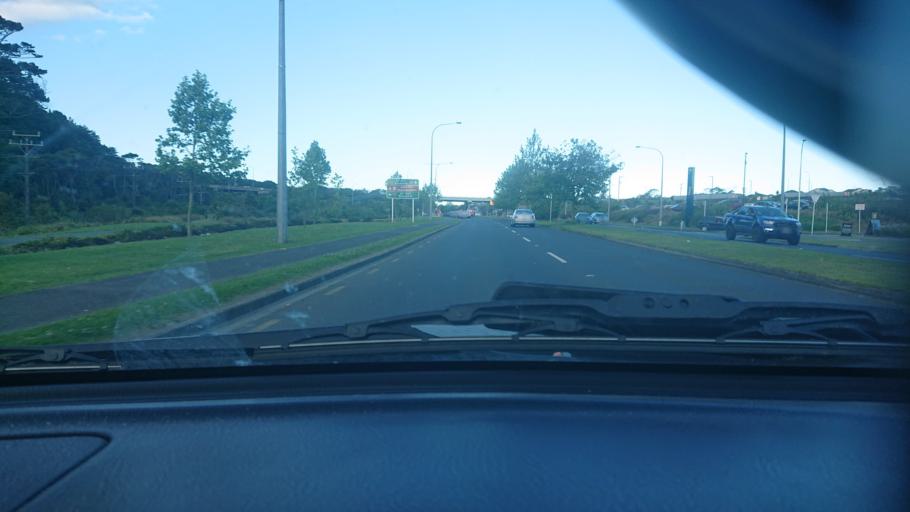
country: NZ
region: Auckland
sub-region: Auckland
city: Rothesay Bay
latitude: -36.7199
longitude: 174.7100
